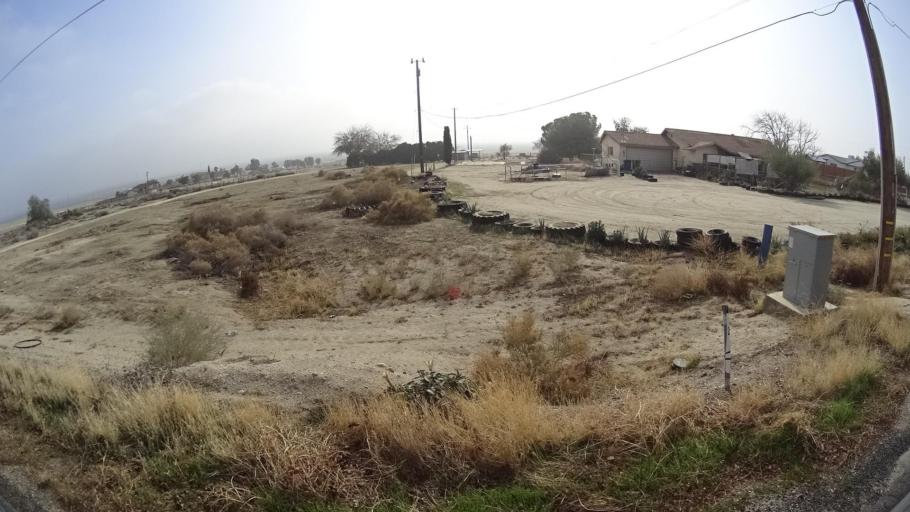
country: US
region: California
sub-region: Kern County
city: Ford City
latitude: 35.2320
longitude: -119.3703
